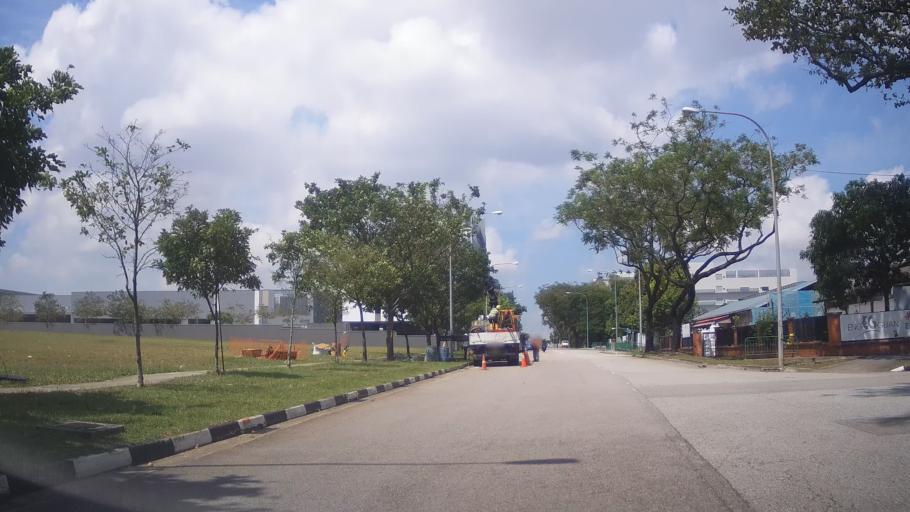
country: SG
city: Singapore
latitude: 1.3264
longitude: 103.7137
